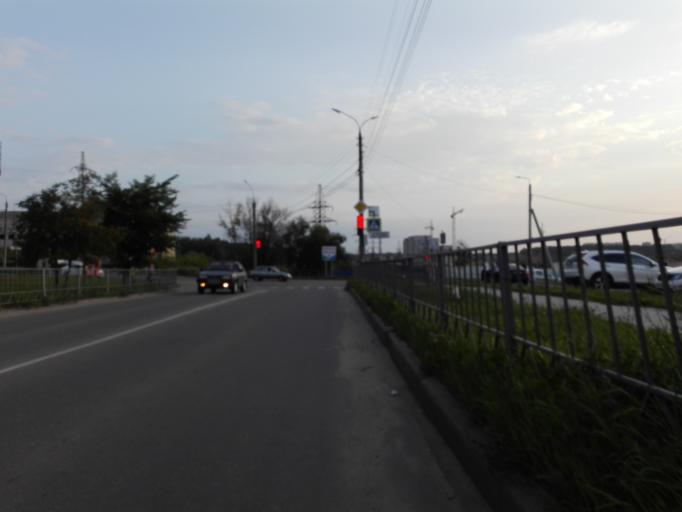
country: RU
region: Orjol
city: Orel
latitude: 53.0083
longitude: 36.1342
